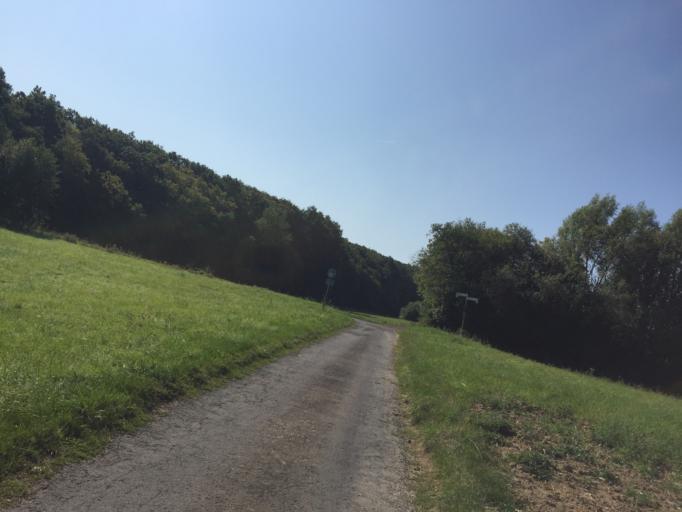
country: DE
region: Hesse
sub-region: Regierungsbezirk Darmstadt
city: Butzbach
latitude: 50.4306
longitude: 8.6008
